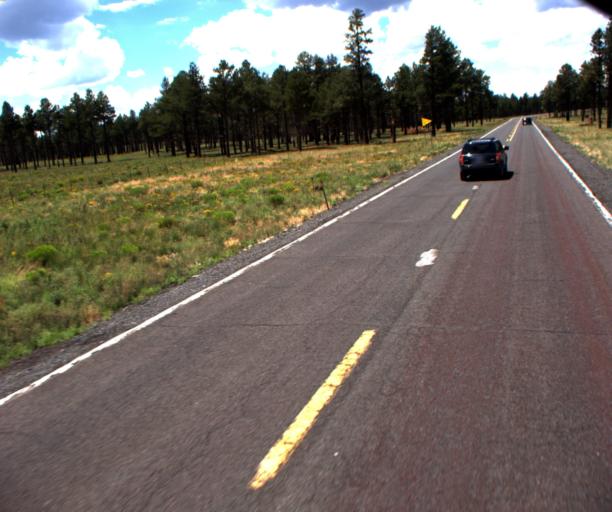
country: US
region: Arizona
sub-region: Coconino County
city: Parks
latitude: 35.4487
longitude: -111.7692
